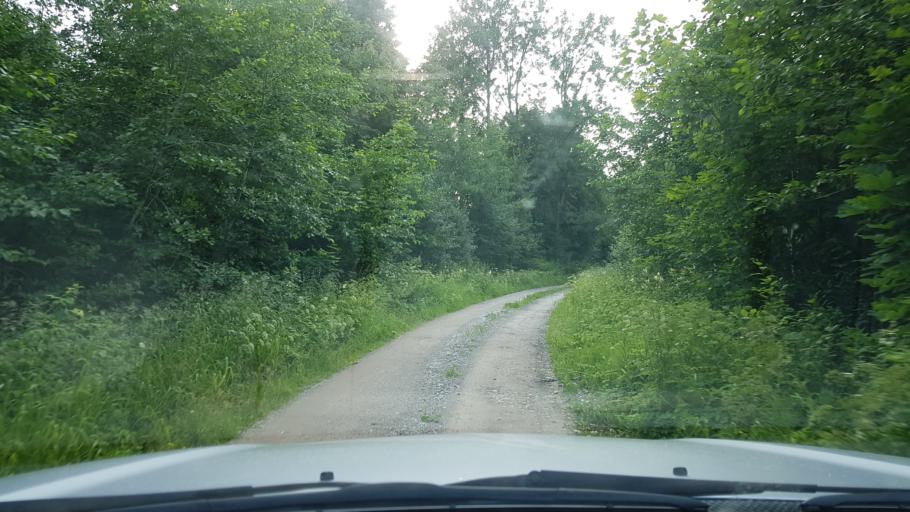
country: EE
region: Ida-Virumaa
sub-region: Narva-Joesuu linn
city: Narva-Joesuu
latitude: 59.4557
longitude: 28.0725
